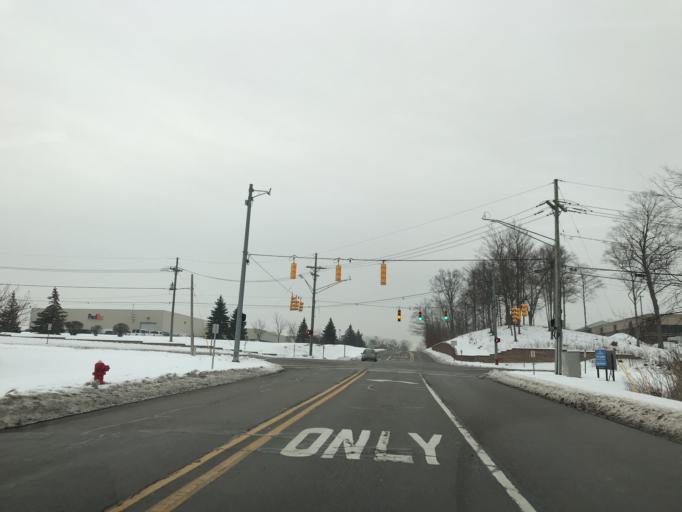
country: US
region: Michigan
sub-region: Oakland County
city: Novi
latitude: 42.4816
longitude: -83.4566
